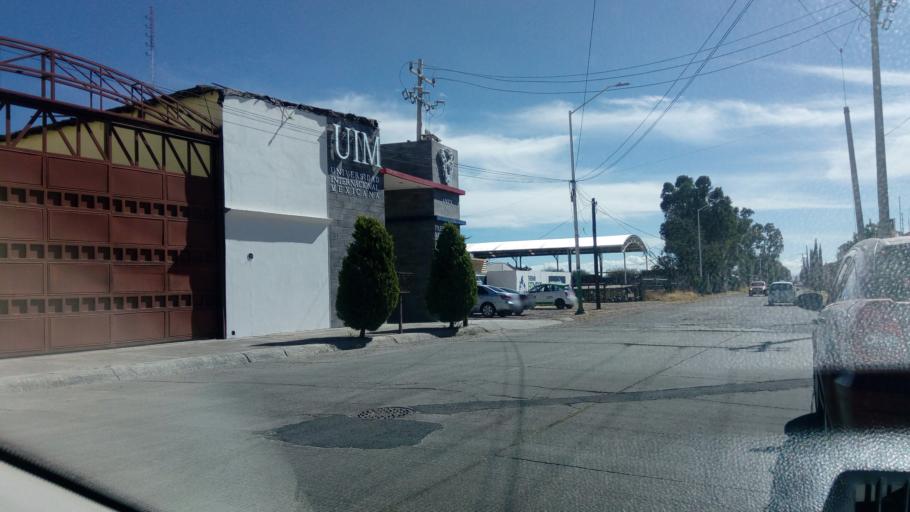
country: MX
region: Durango
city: Victoria de Durango
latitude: 24.0524
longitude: -104.6303
